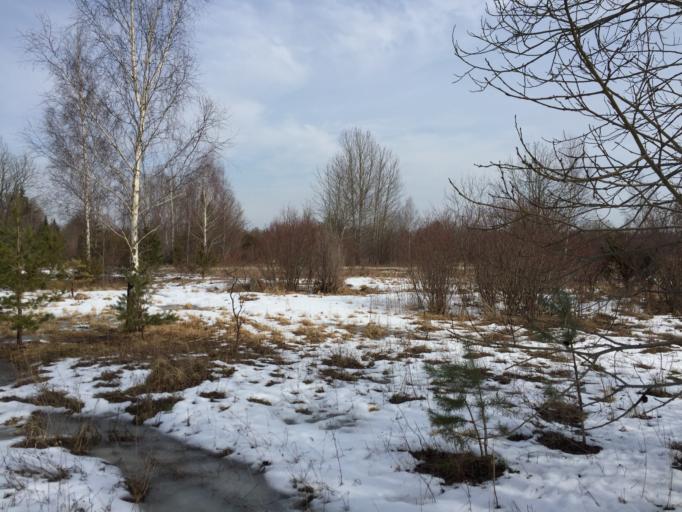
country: EE
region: Saare
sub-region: Kuressaare linn
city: Kuressaare
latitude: 58.3383
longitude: 22.4712
